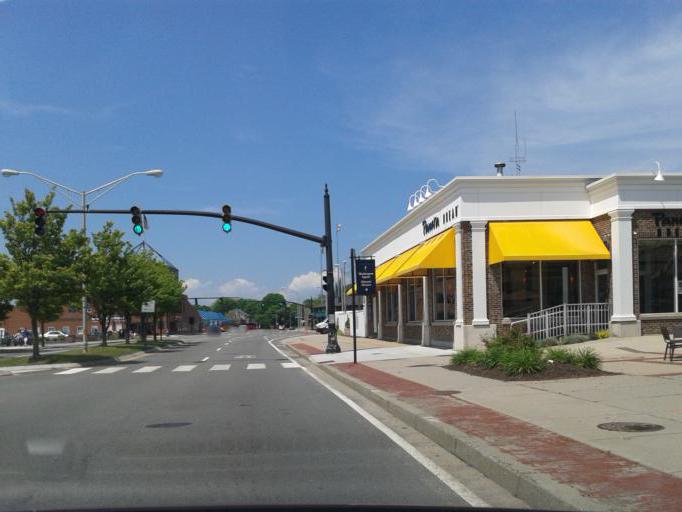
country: US
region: Rhode Island
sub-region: Newport County
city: Newport
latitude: 41.4895
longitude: -71.3169
